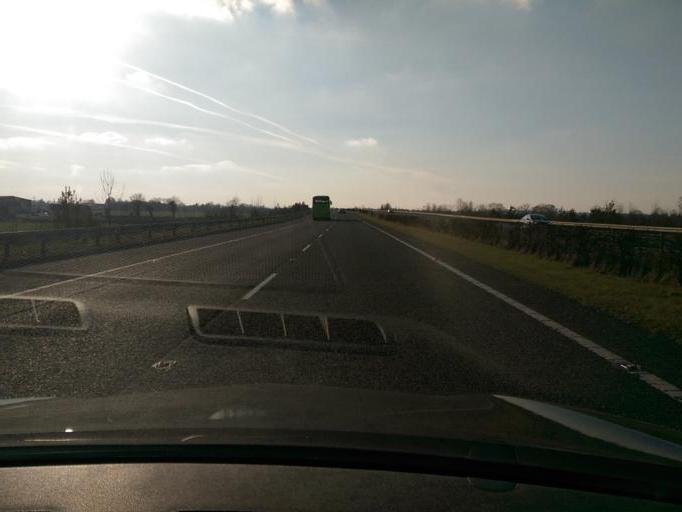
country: IE
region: Leinster
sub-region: Kildare
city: Monasterevin
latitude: 53.1142
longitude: -7.0793
